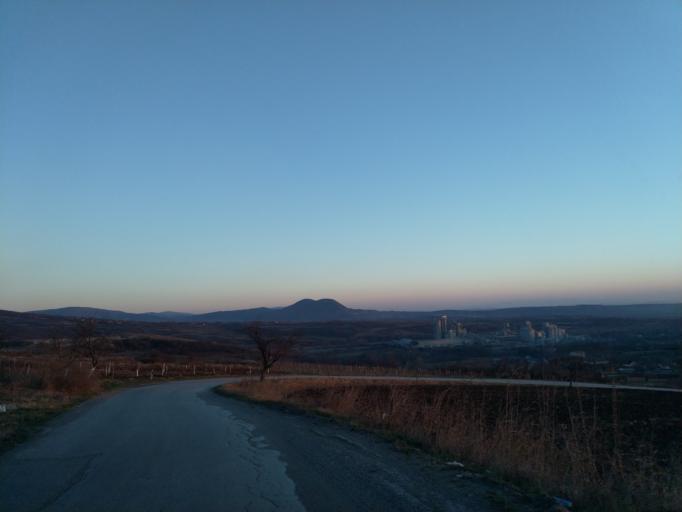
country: RS
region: Central Serbia
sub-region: Pomoravski Okrug
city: Paracin
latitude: 43.9253
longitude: 21.5112
